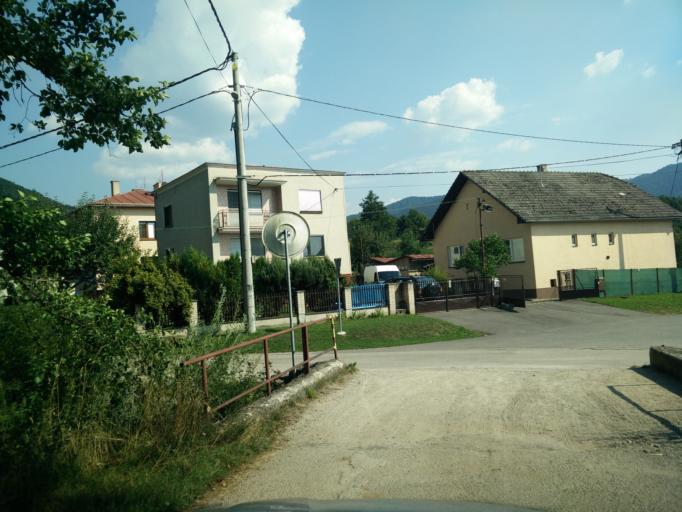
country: SK
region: Zilinsky
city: Rajec
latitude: 49.1029
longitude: 18.7100
